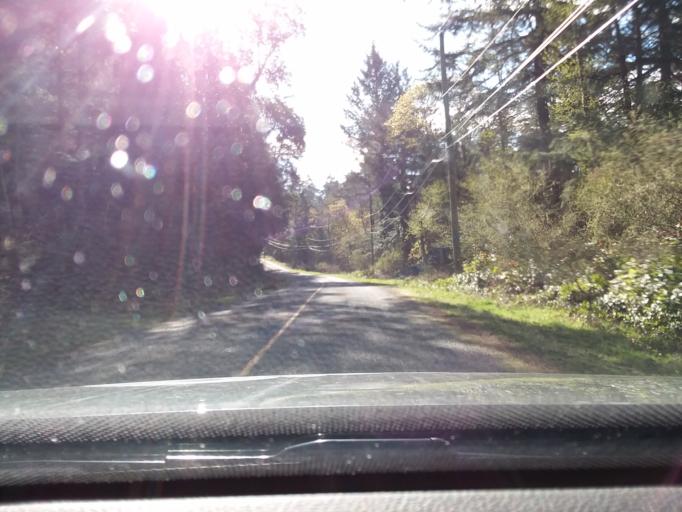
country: CA
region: British Columbia
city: North Cowichan
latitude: 48.9508
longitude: -123.5286
